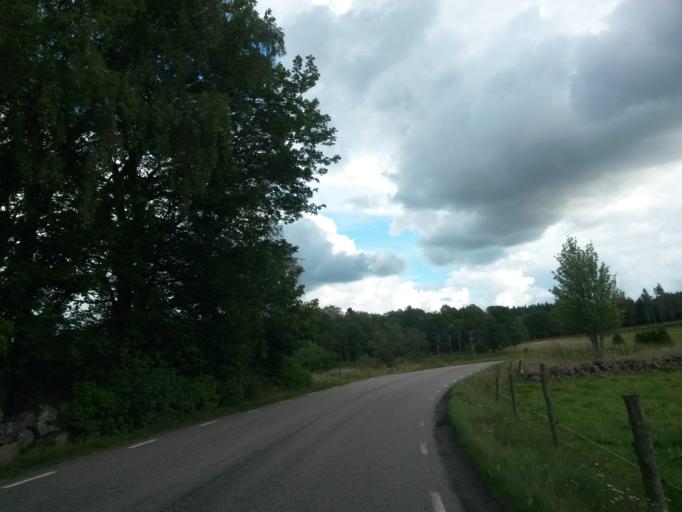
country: SE
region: Vaestra Goetaland
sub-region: Vargarda Kommun
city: Vargarda
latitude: 57.9893
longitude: 12.7965
